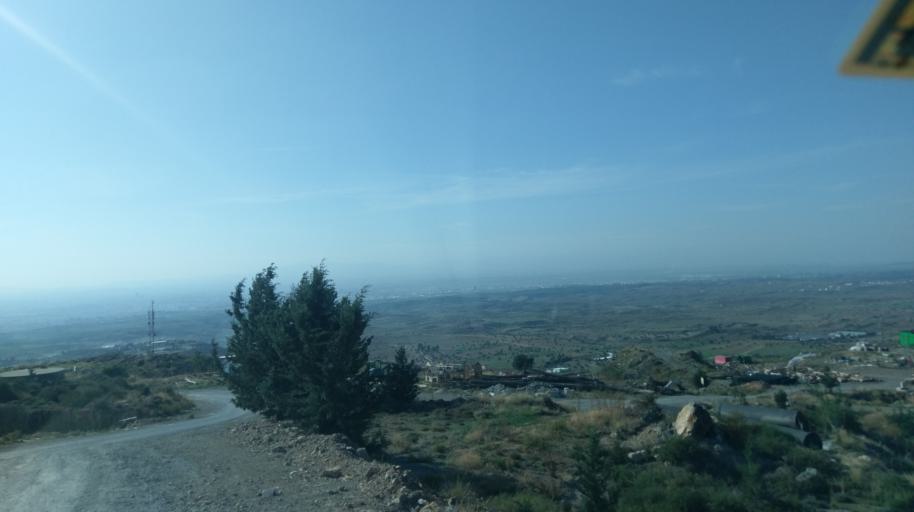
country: CY
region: Keryneia
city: Kyrenia
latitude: 35.2790
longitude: 33.3841
